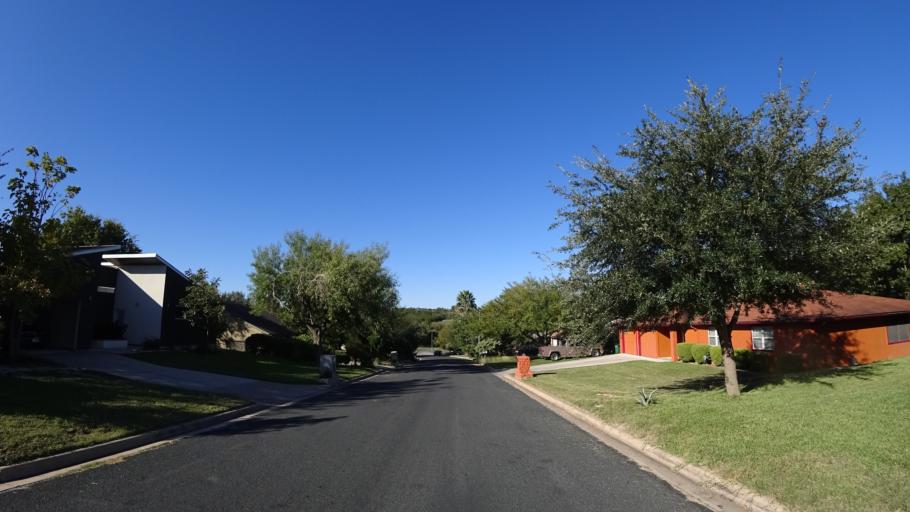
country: US
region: Texas
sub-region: Travis County
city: Austin
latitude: 30.3061
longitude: -97.6659
